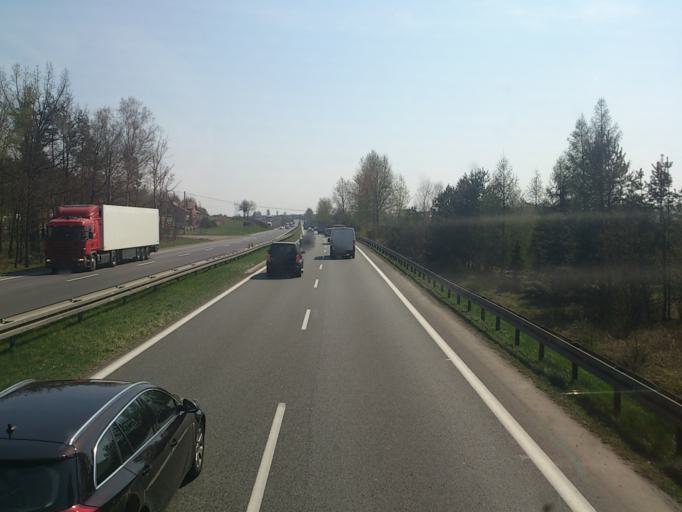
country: PL
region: Silesian Voivodeship
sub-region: Powiat bedzinski
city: Siewierz
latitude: 50.5180
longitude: 19.1938
